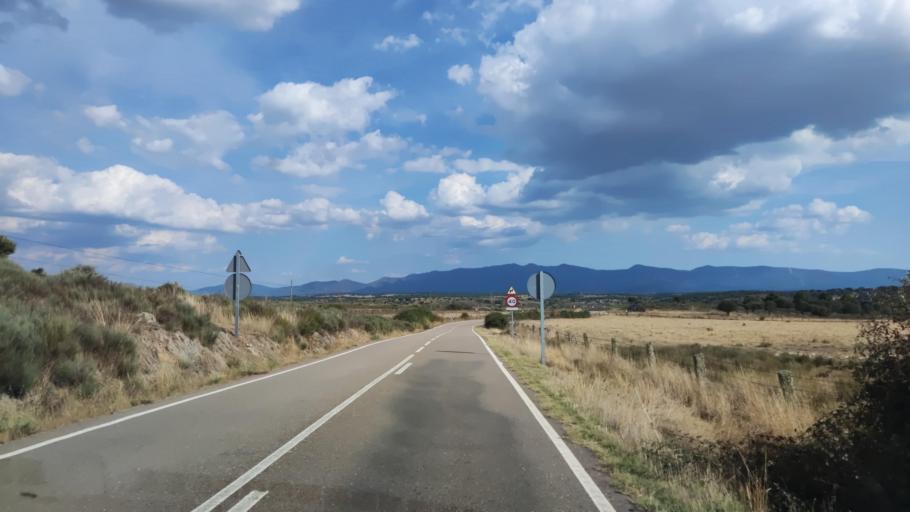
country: ES
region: Castille and Leon
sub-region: Provincia de Salamanca
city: Pastores
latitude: 40.5038
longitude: -6.5019
